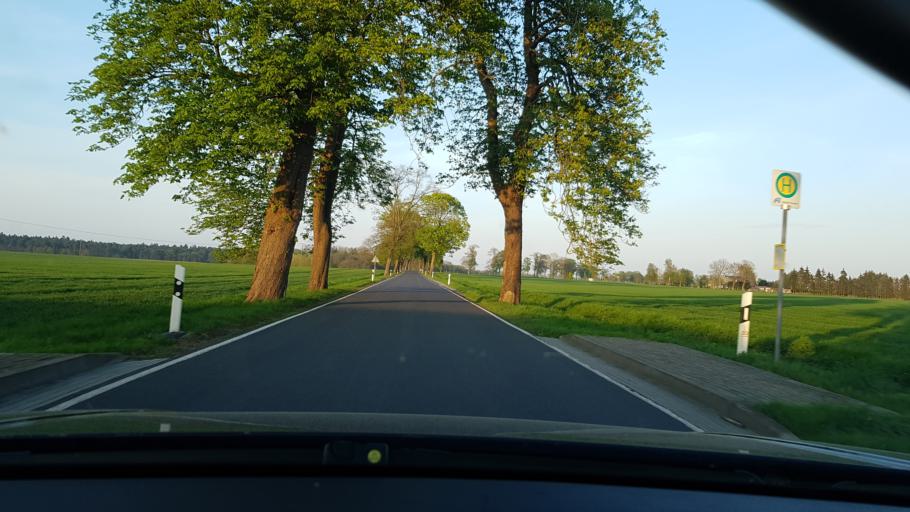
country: DE
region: Mecklenburg-Vorpommern
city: Anklam
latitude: 53.8862
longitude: 13.6404
